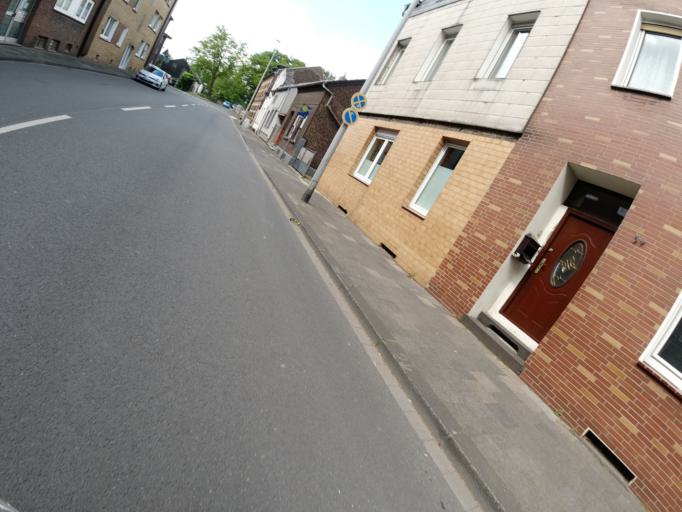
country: DE
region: North Rhine-Westphalia
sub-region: Regierungsbezirk Dusseldorf
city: Hochfeld
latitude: 51.3949
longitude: 6.6953
